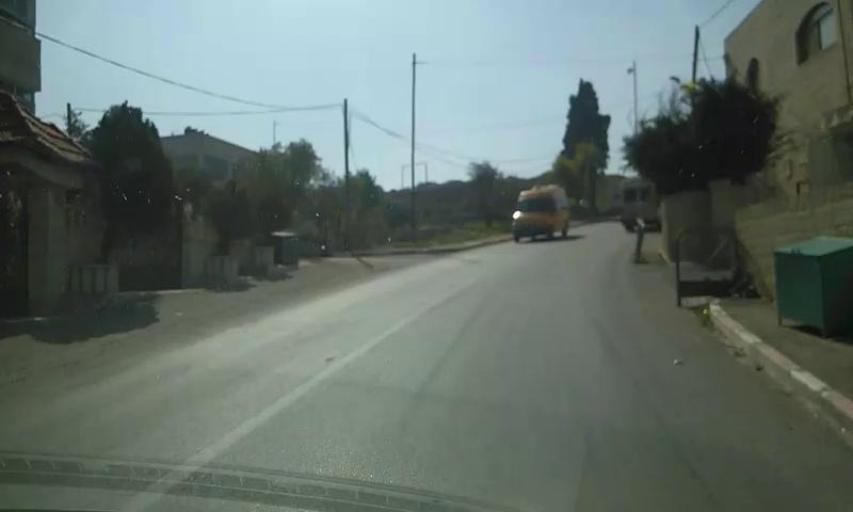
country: PS
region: West Bank
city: At Taybah
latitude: 31.9595
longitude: 35.2970
